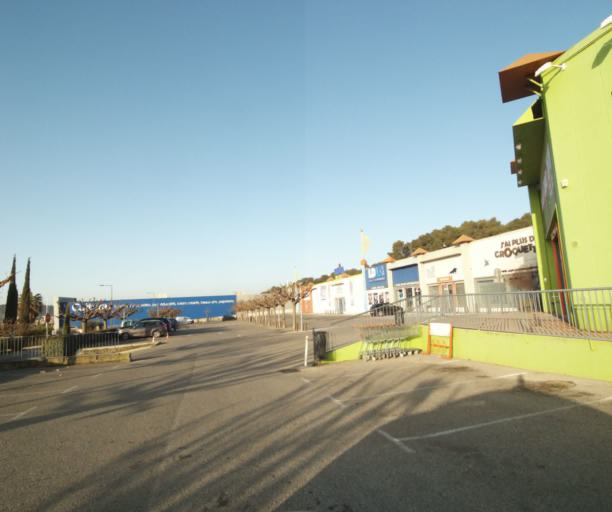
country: FR
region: Provence-Alpes-Cote d'Azur
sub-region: Departement des Bouches-du-Rhone
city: Cabries
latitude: 43.4232
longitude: 5.3647
